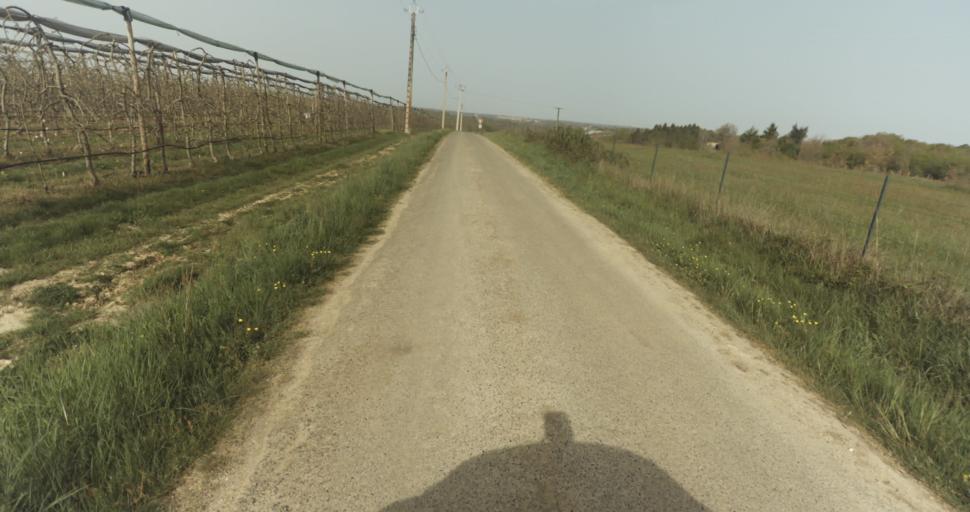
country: FR
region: Midi-Pyrenees
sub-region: Departement du Tarn-et-Garonne
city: Moissac
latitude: 44.1524
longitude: 1.0673
